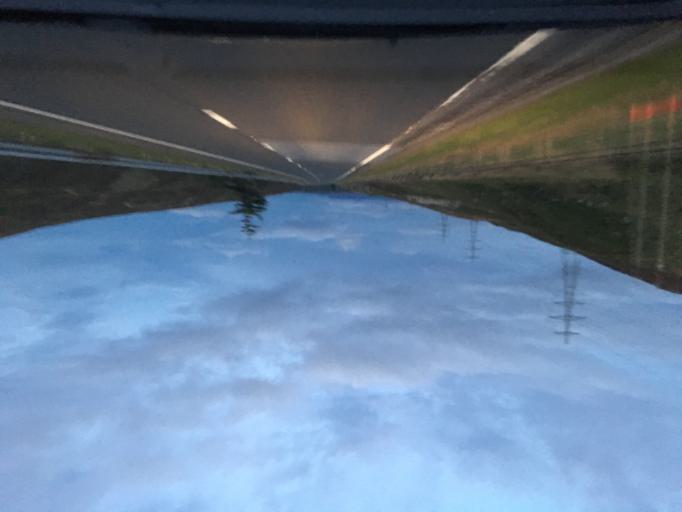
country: GB
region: Scotland
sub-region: Highland
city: Kingussie
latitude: 56.8180
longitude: -4.1677
